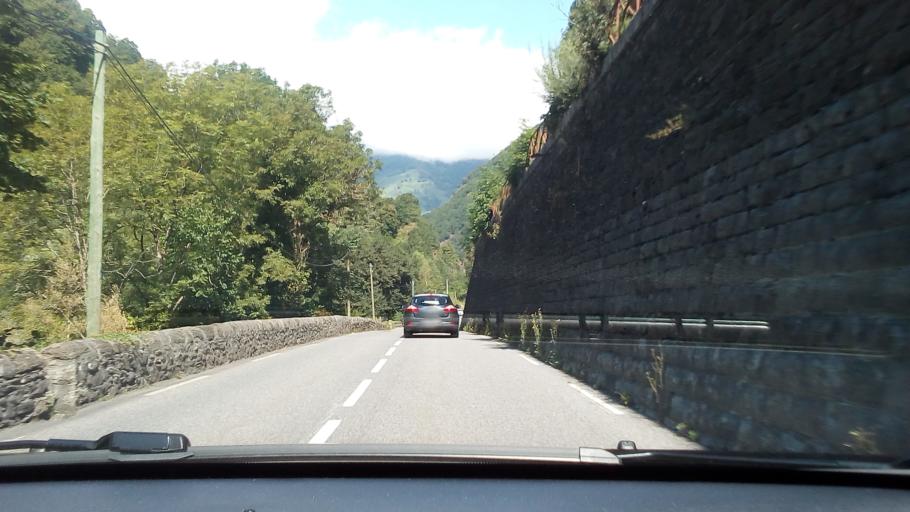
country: FR
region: Aquitaine
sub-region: Departement des Pyrenees-Atlantiques
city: Laruns
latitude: 42.9315
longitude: -0.5833
